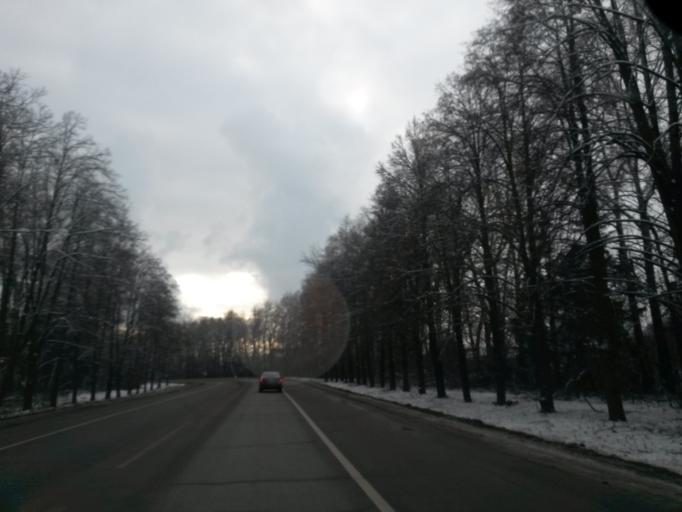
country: RU
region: Moskovskaya
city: Stolbovaya
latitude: 55.2502
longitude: 37.5041
